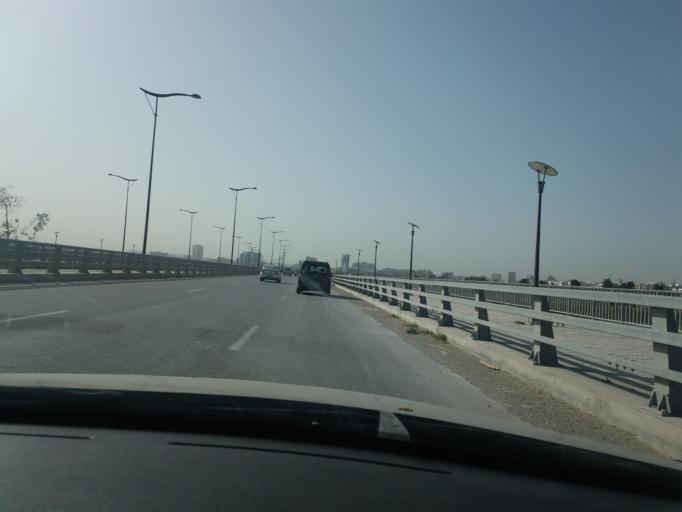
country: TN
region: Tunis
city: Tunis
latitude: 36.8209
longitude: 10.2002
